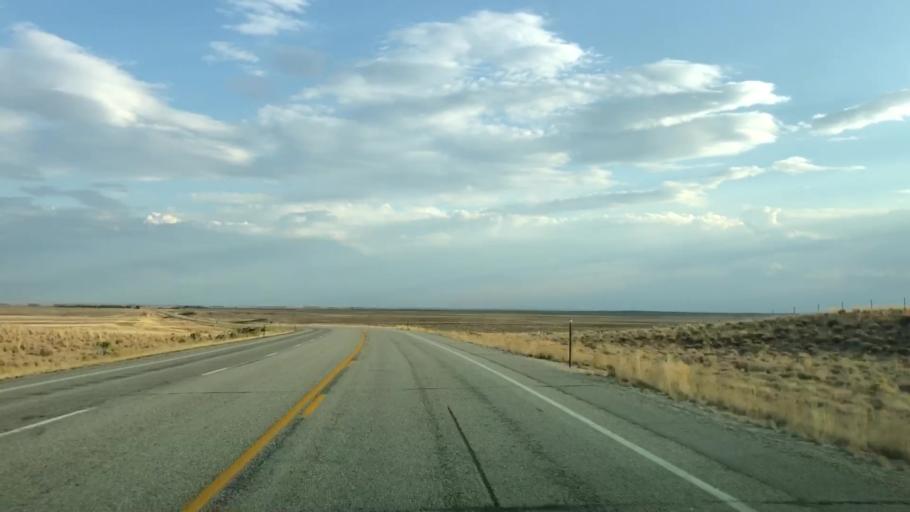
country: US
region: Wyoming
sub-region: Sweetwater County
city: North Rock Springs
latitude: 42.1918
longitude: -109.4811
